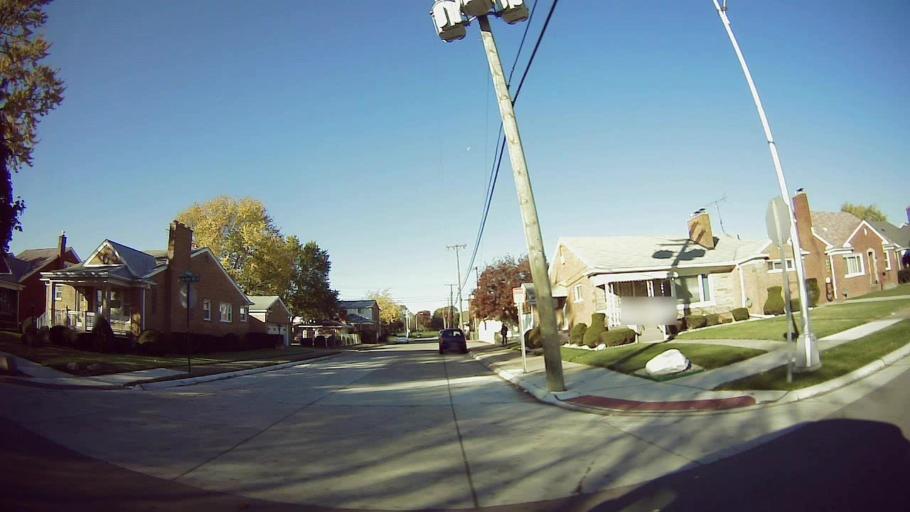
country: US
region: Michigan
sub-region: Wayne County
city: Dearborn
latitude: 42.3315
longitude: -83.1692
